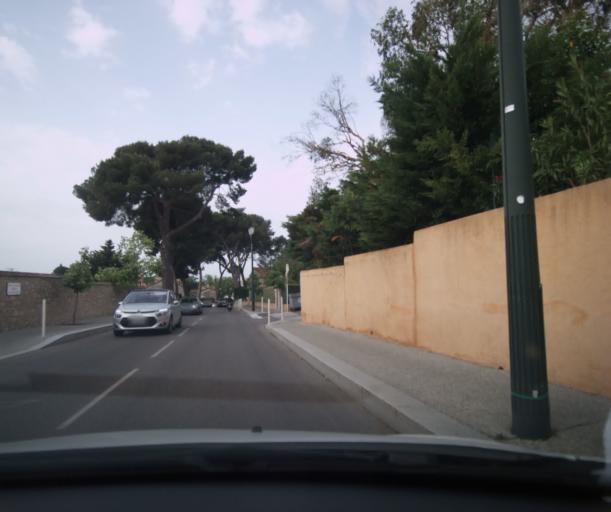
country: FR
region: Provence-Alpes-Cote d'Azur
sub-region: Departement du Var
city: Carqueiranne
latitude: 43.0957
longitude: 6.0776
